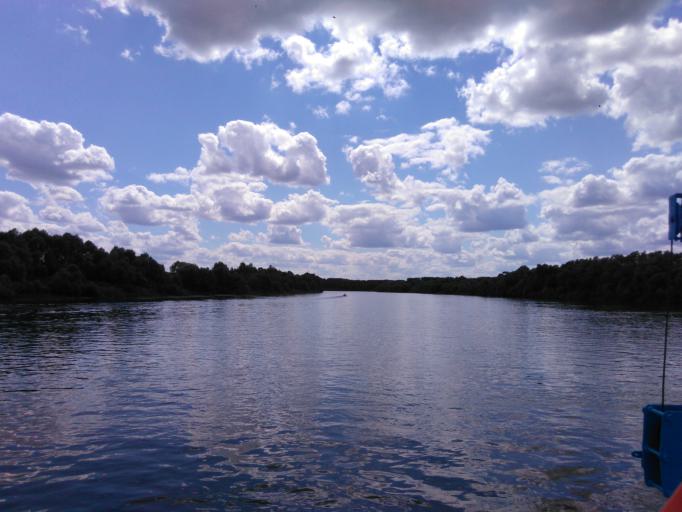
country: RU
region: Rjazan
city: Polyany
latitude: 54.6607
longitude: 39.7892
